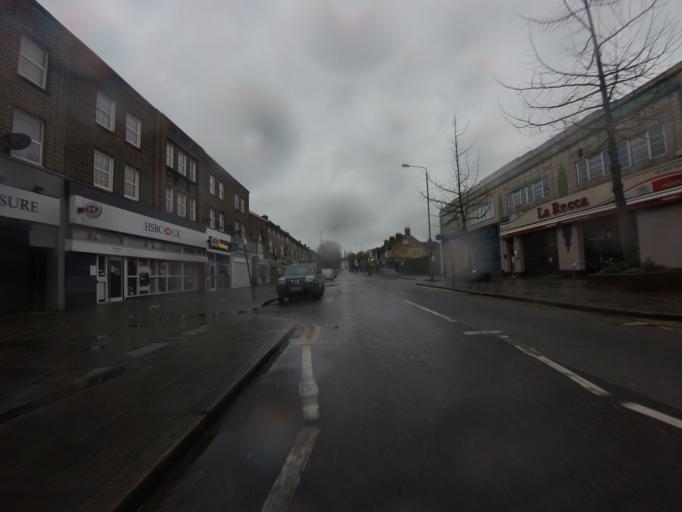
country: GB
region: England
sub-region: Greater London
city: Walthamstow
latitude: 51.6184
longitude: -0.0174
